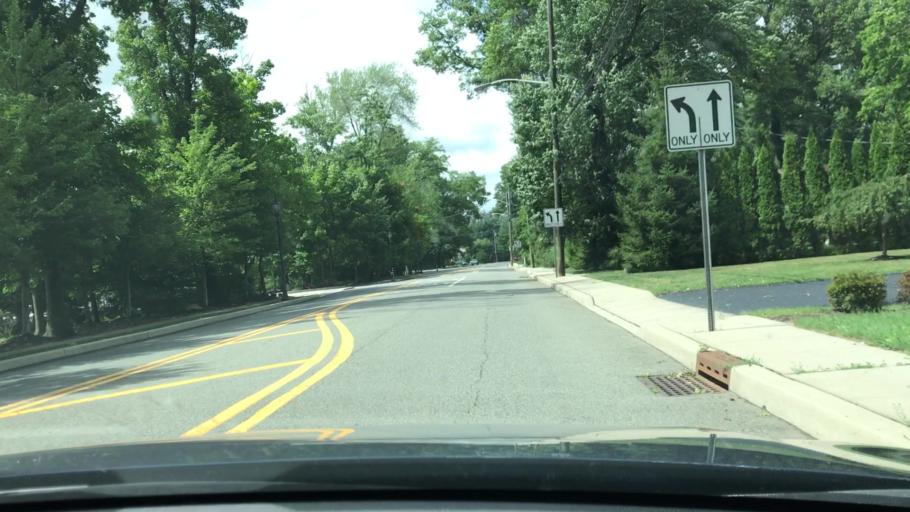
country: US
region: New Jersey
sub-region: Bergen County
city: Wyckoff
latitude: 41.0130
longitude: -74.1655
